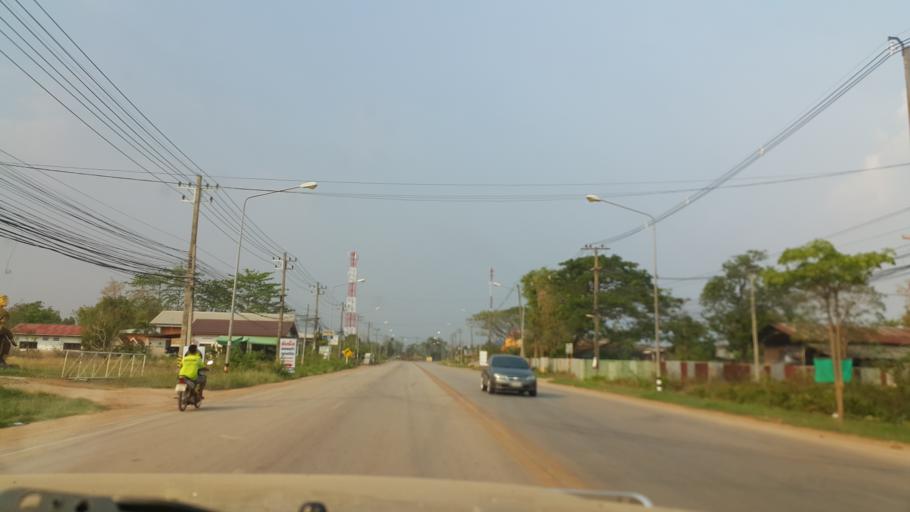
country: TH
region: Nakhon Phanom
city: That Phanom
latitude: 16.9517
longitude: 104.7220
